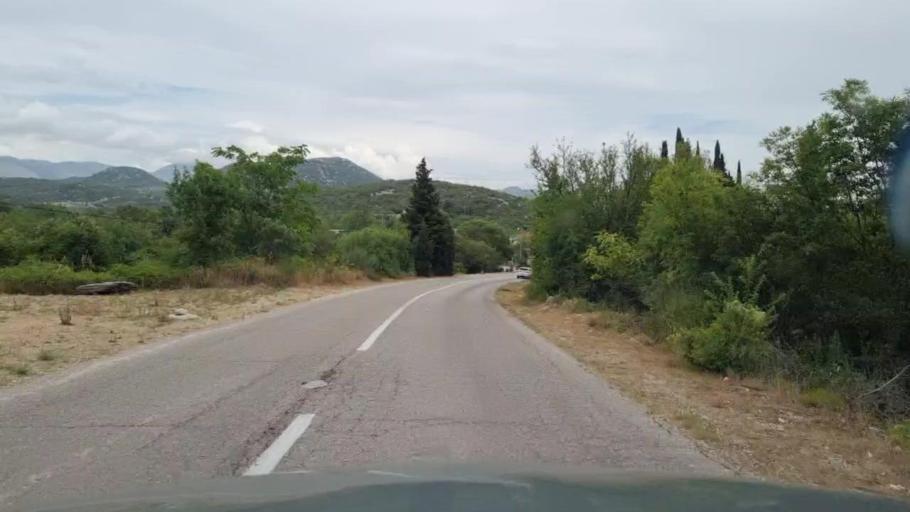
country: BA
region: Federation of Bosnia and Herzegovina
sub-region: Hercegovacko-Bosanski Kanton
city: Neum
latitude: 42.9229
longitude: 17.6400
